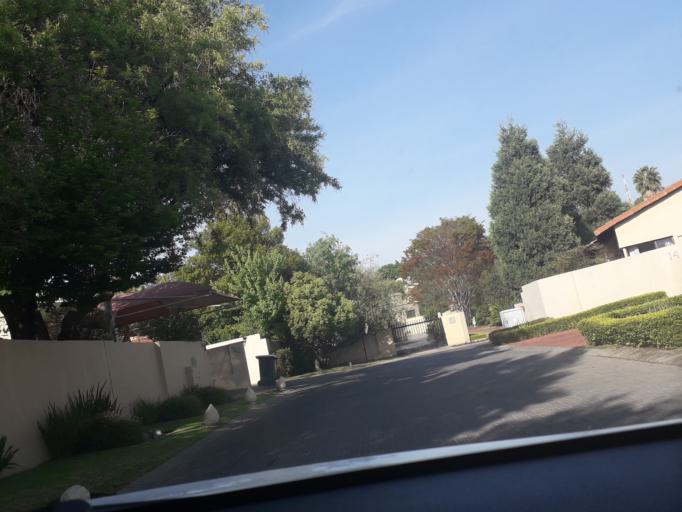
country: ZA
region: Gauteng
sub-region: City of Johannesburg Metropolitan Municipality
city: Diepsloot
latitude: -26.0458
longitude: 27.9811
